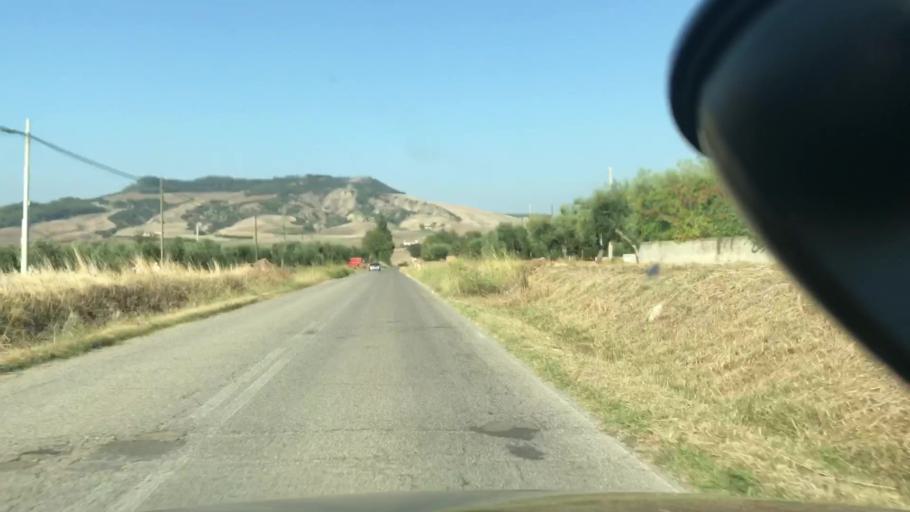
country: IT
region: Basilicate
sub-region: Provincia di Matera
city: La Martella
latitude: 40.6583
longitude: 16.5269
